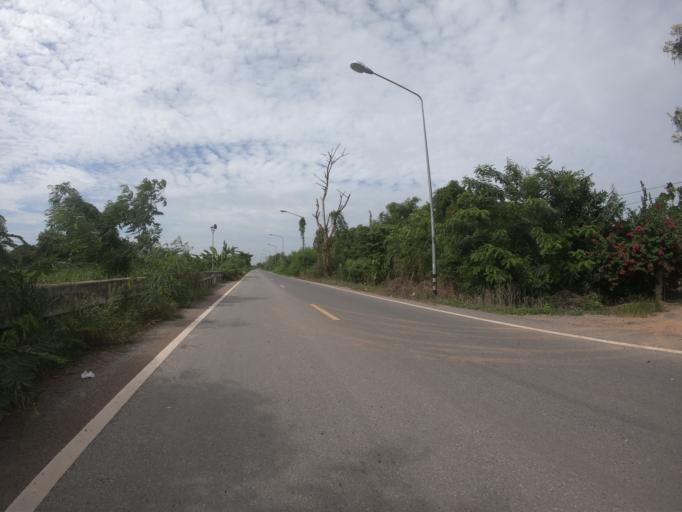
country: TH
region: Pathum Thani
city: Nong Suea
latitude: 14.0462
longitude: 100.8929
